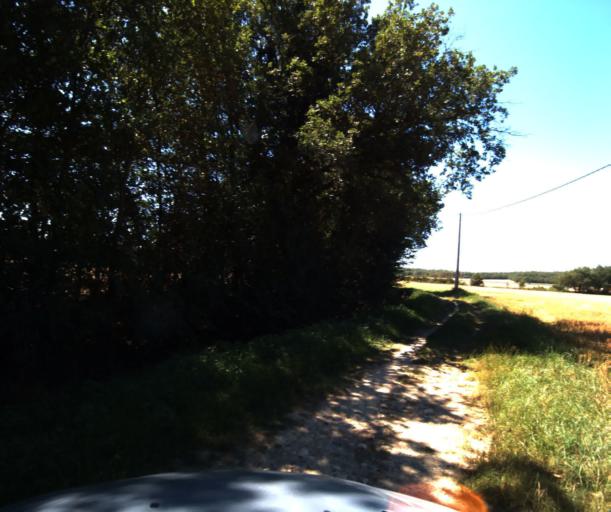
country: FR
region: Midi-Pyrenees
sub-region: Departement de la Haute-Garonne
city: Muret
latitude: 43.4473
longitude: 1.3584
